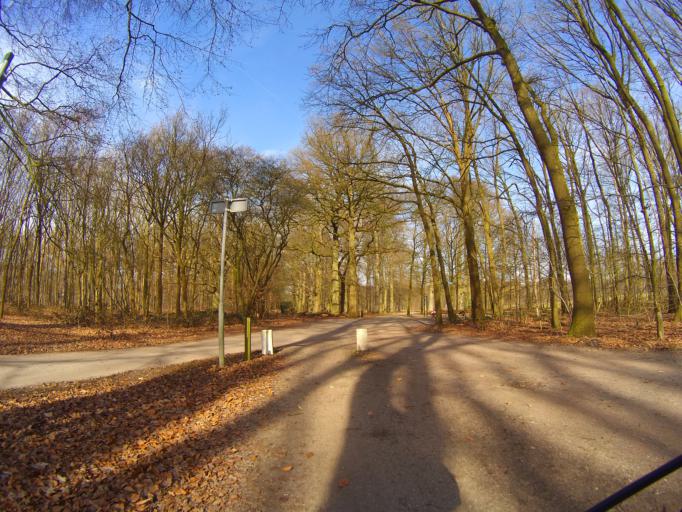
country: NL
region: Utrecht
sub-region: Gemeente Baarn
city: Baarn
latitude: 52.2142
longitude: 5.2430
